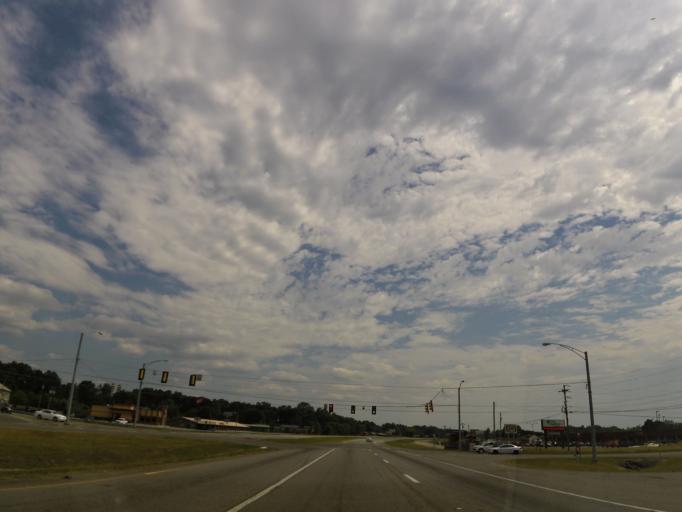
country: US
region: Alabama
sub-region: Jackson County
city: Stevenson
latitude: 34.8738
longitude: -85.8129
